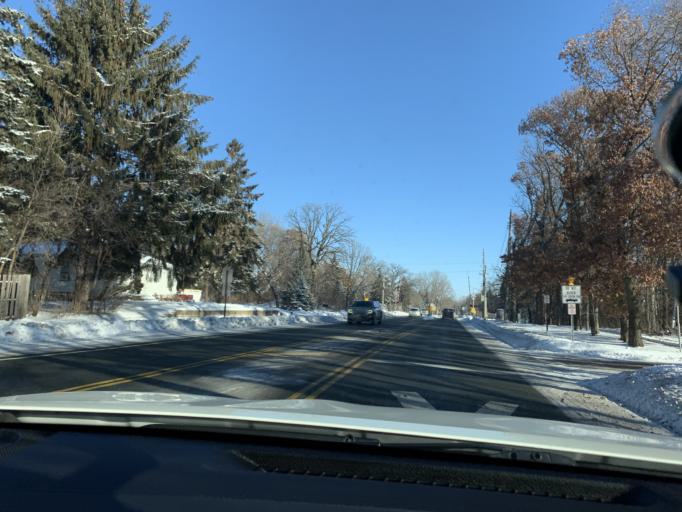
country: US
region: Minnesota
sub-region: Anoka County
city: Coon Rapids
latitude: 45.1564
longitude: -93.3045
